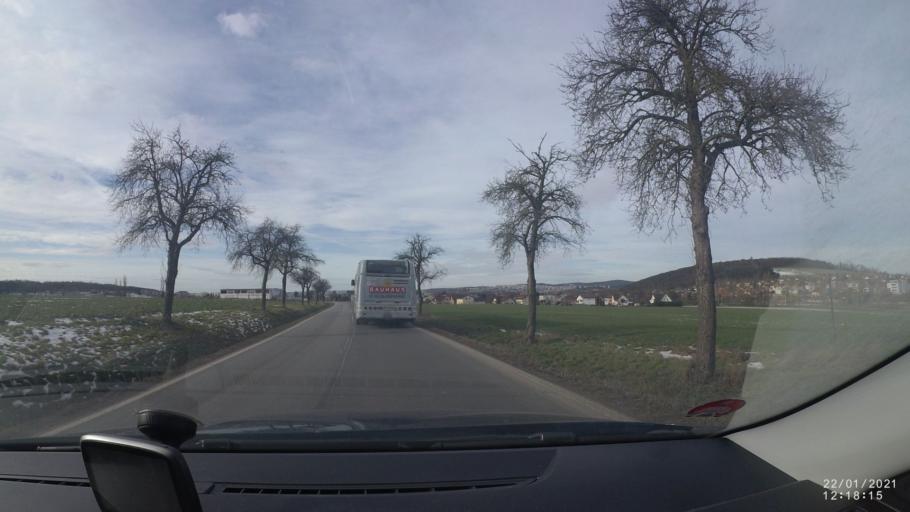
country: CZ
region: Plzensky
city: Dysina
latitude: 49.7569
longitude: 13.4423
